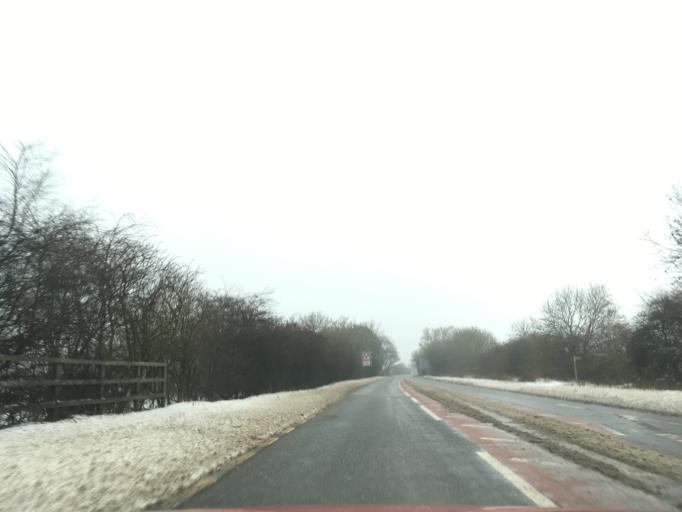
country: GB
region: England
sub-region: Worcestershire
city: Evesham
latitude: 52.0381
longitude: -1.9900
